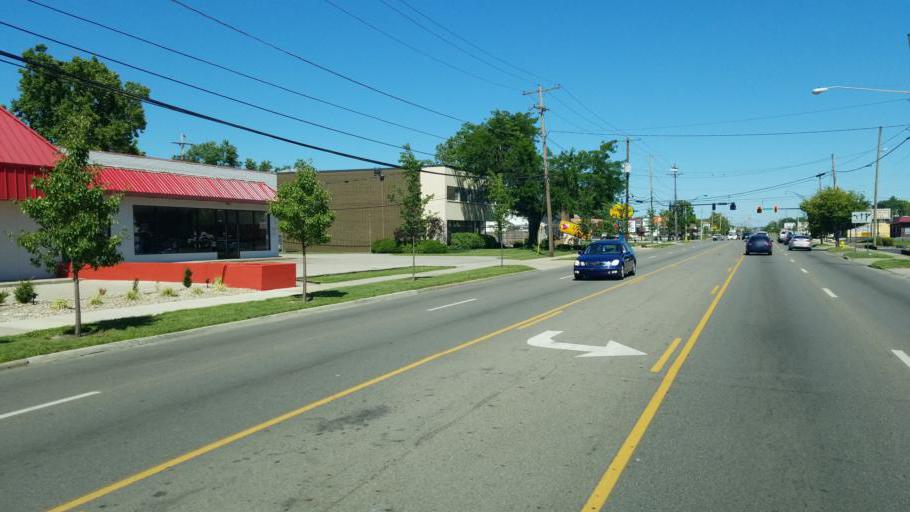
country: US
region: Ohio
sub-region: Franklin County
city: Whitehall
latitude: 39.9558
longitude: -82.8882
